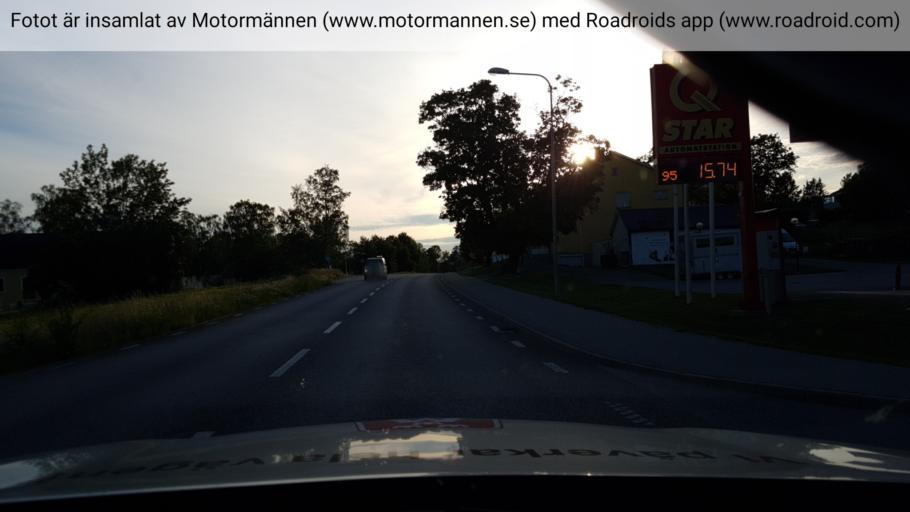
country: SE
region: OErebro
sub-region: Lindesbergs Kommun
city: Lindesberg
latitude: 59.5271
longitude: 15.2854
